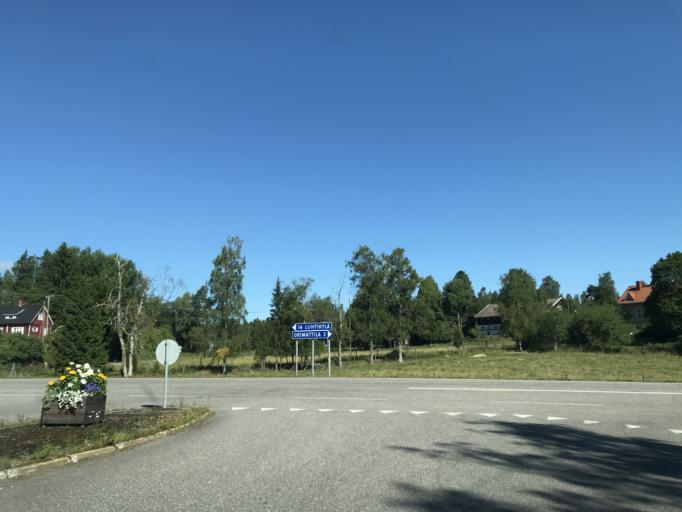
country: FI
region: Paijanne Tavastia
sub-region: Lahti
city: Orimattila
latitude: 60.8103
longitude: 25.6833
